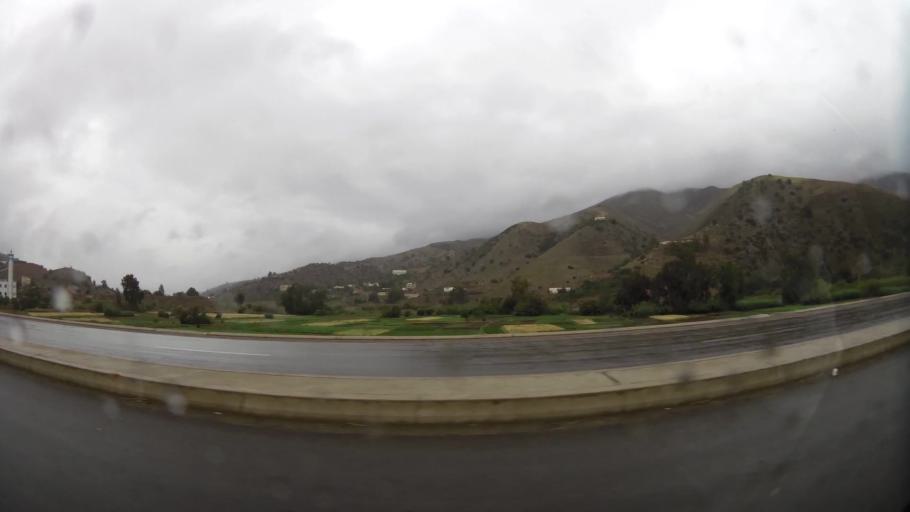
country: MA
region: Taza-Al Hoceima-Taounate
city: Imzourene
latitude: 35.0156
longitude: -3.8187
